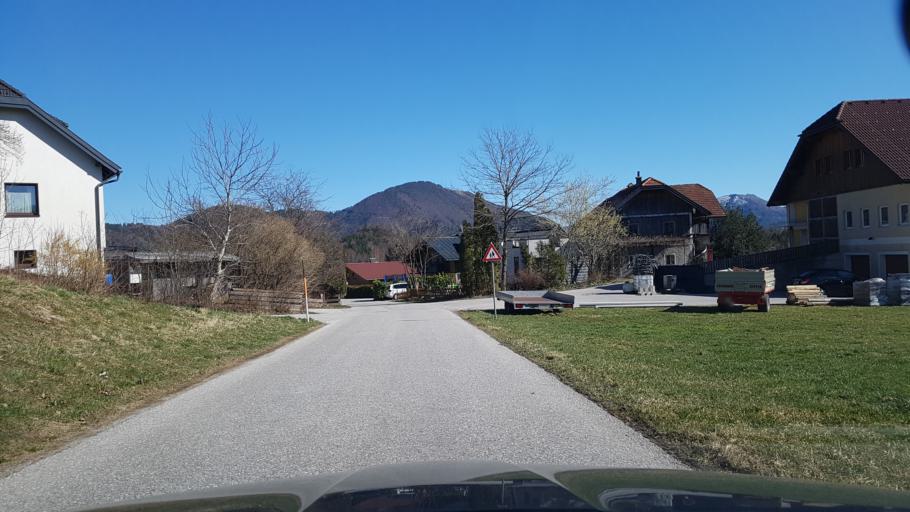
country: AT
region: Salzburg
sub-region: Politischer Bezirk Salzburg-Umgebung
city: Koppl
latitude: 47.8036
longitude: 13.1670
